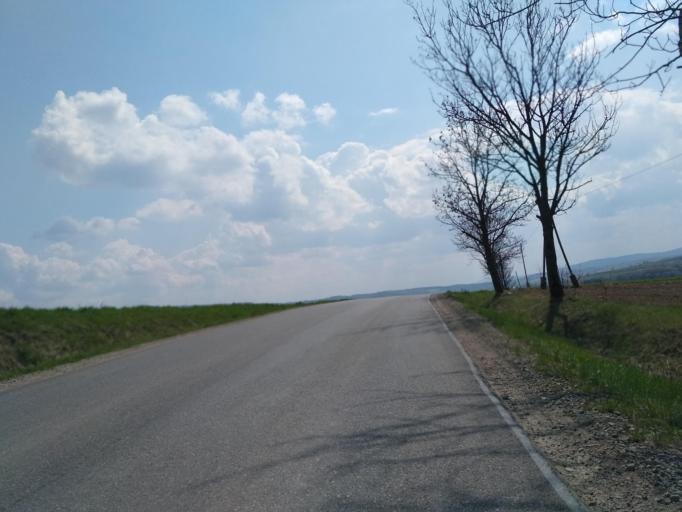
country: PL
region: Subcarpathian Voivodeship
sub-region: Powiat sanocki
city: Bukowsko
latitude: 49.4958
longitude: 22.0425
